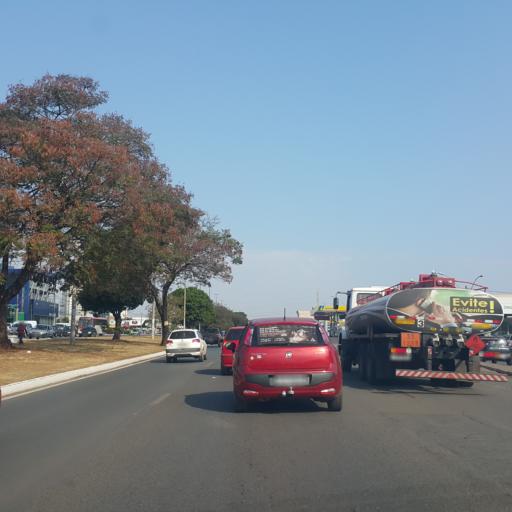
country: BR
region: Federal District
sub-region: Brasilia
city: Brasilia
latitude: -15.8476
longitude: -48.0431
